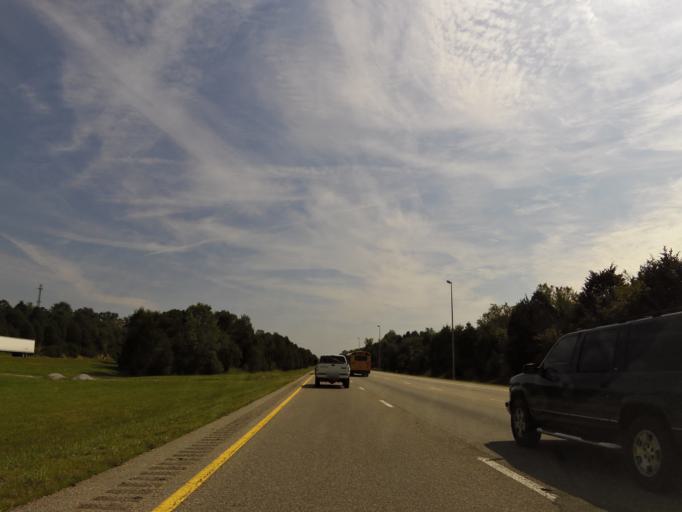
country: US
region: Tennessee
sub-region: Greene County
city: Mosheim
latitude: 36.2258
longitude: -83.0350
